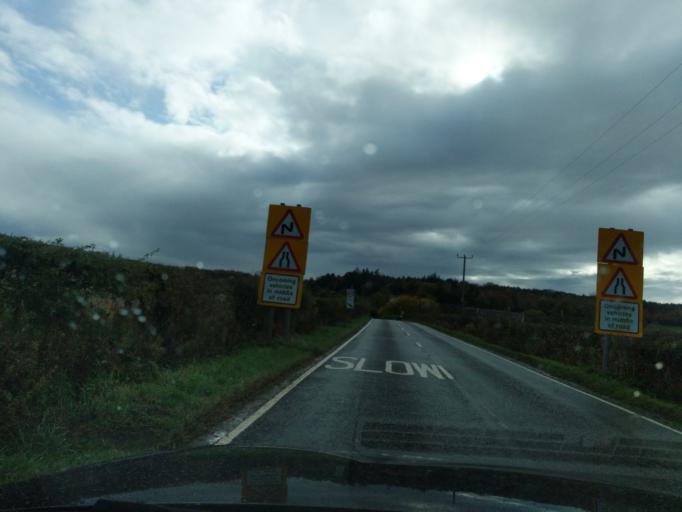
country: GB
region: Scotland
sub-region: Fife
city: Saint Andrews
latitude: 56.2973
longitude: -2.7523
